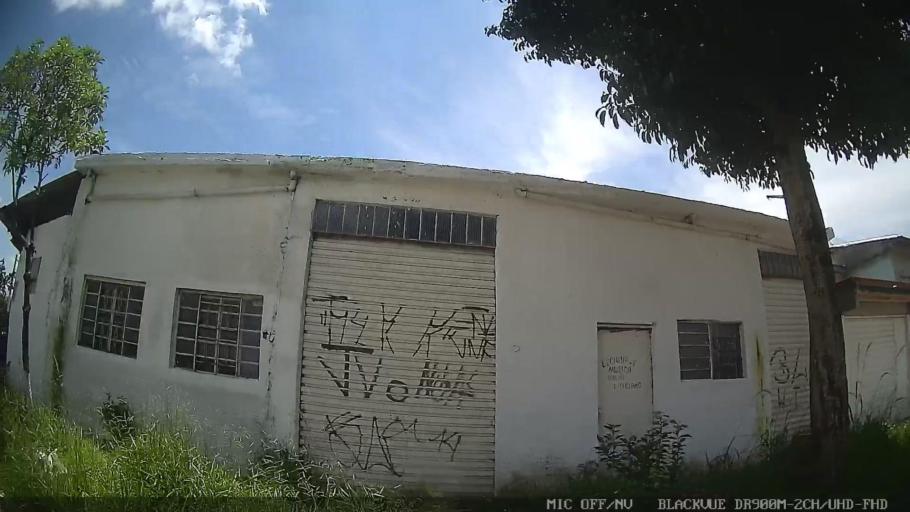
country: BR
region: Sao Paulo
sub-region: Suzano
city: Suzano
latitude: -23.5323
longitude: -46.3211
